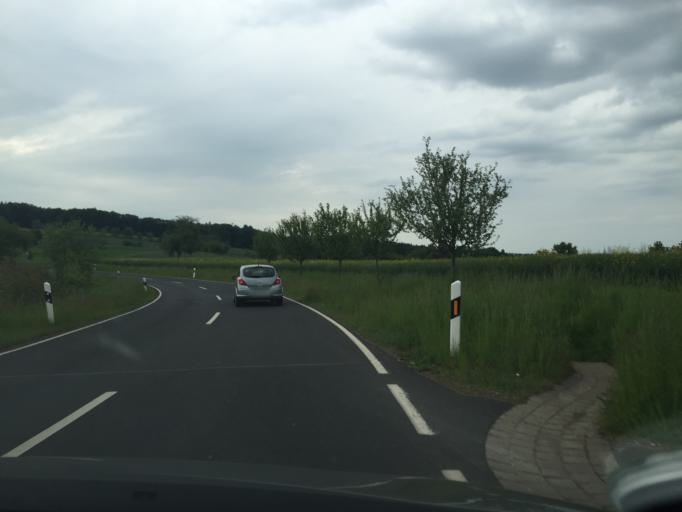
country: DE
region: Bavaria
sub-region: Regierungsbezirk Unterfranken
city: Johannesberg
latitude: 50.0367
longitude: 9.1147
